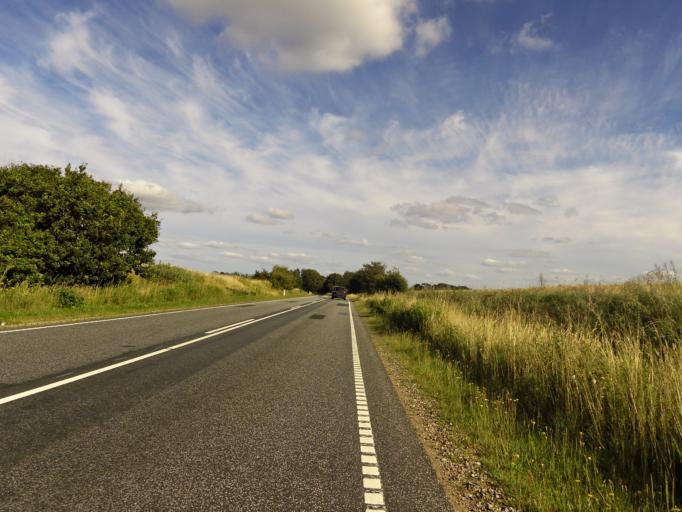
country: DK
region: South Denmark
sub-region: Tonder Kommune
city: Toftlund
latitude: 55.2200
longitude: 9.0149
